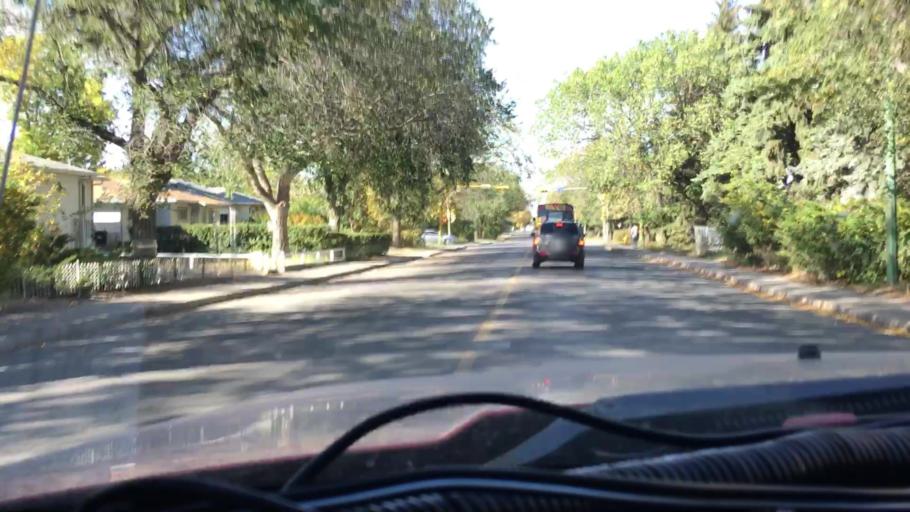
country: CA
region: Saskatchewan
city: Regina
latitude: 50.4621
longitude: -104.6312
